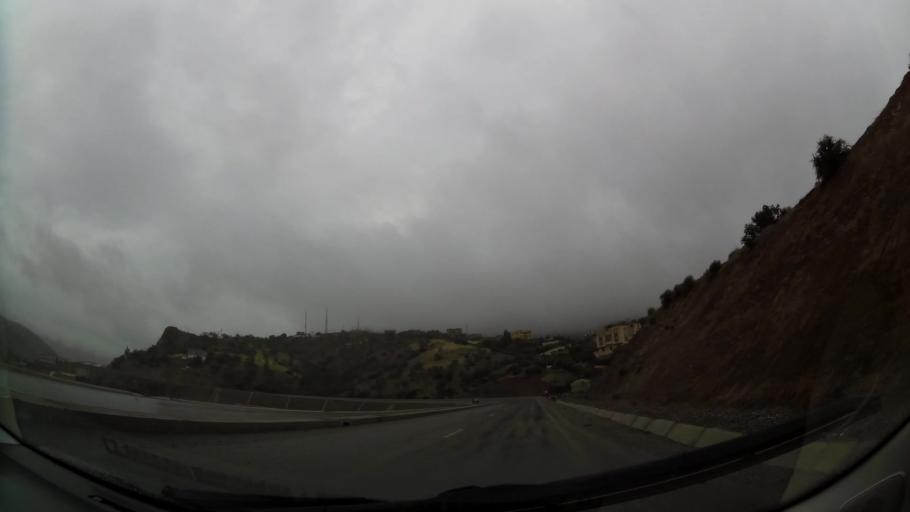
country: MA
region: Taza-Al Hoceima-Taounate
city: Imzourene
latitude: 35.0340
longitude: -3.8222
